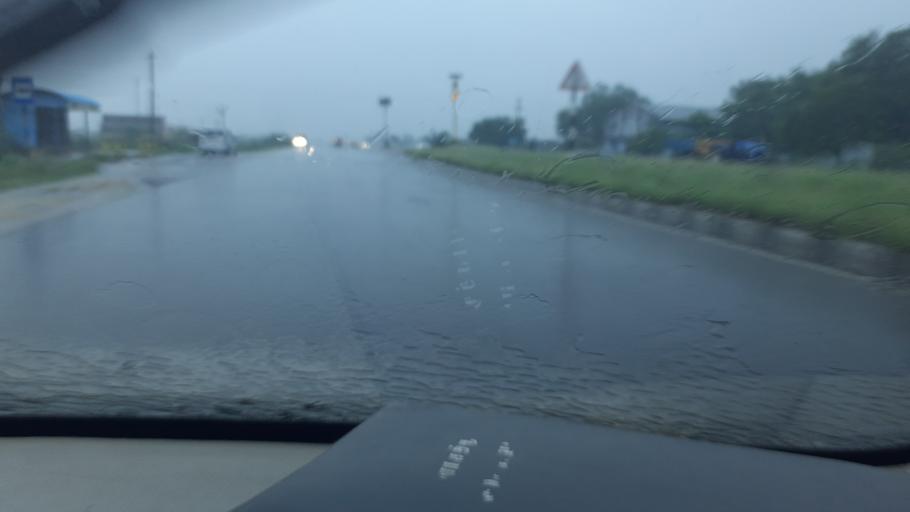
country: IN
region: Tamil Nadu
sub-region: Virudhunagar
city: Sattur
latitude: 9.4256
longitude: 77.9181
